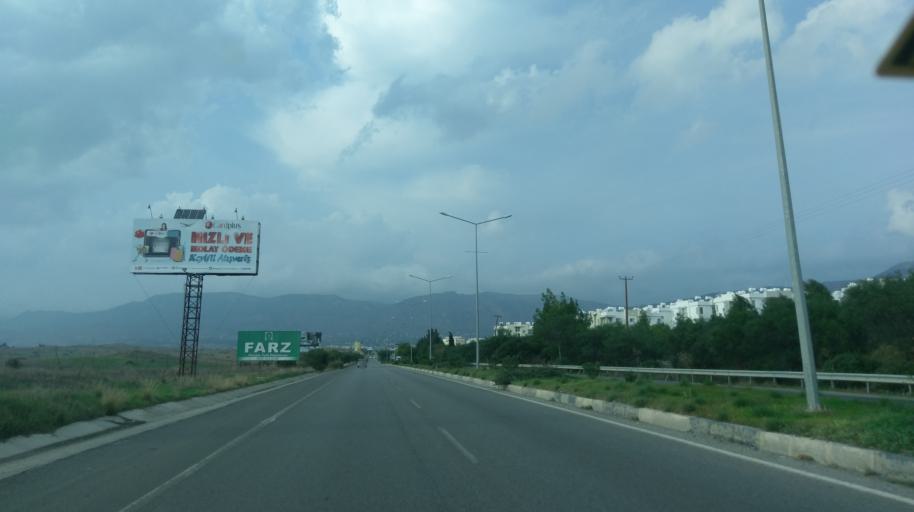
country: CY
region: Keryneia
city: Kyrenia
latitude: 35.2535
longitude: 33.3016
